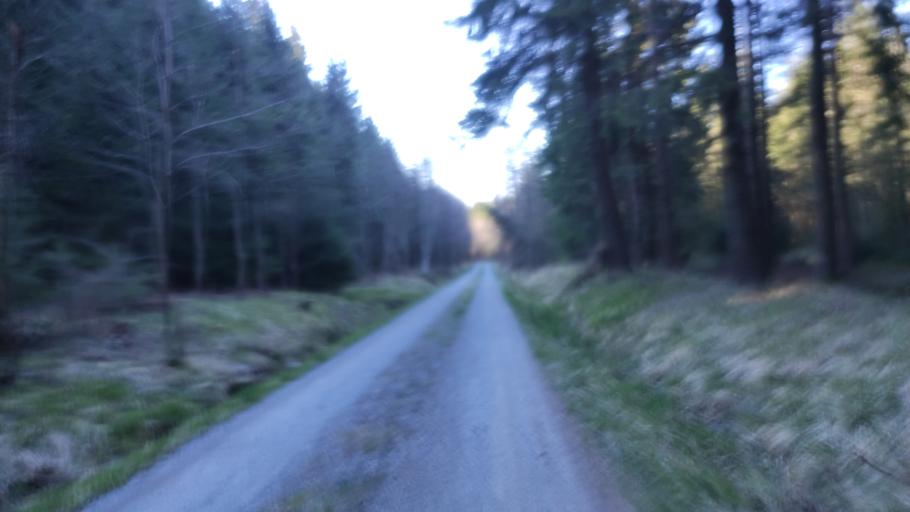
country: DE
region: Bavaria
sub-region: Upper Franconia
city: Reichenbach
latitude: 50.4468
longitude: 11.4375
